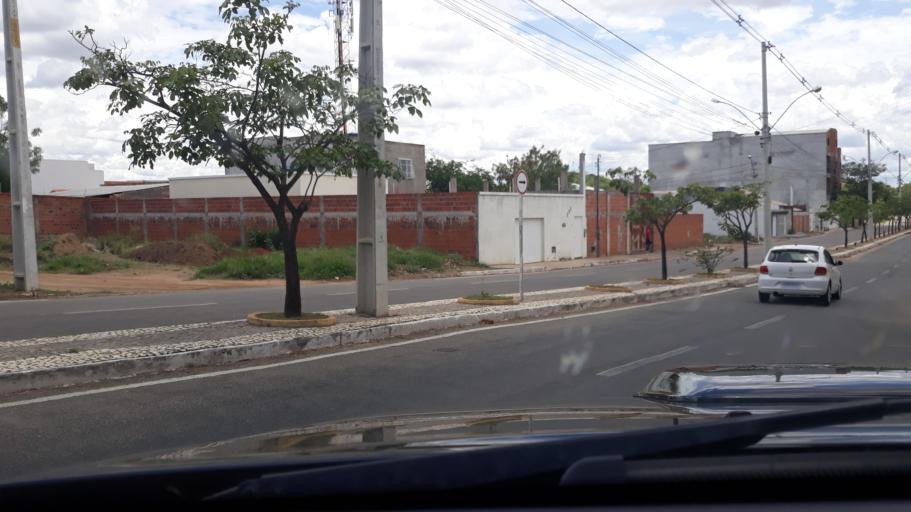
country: BR
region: Bahia
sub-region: Guanambi
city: Guanambi
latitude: -14.2267
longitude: -42.7687
